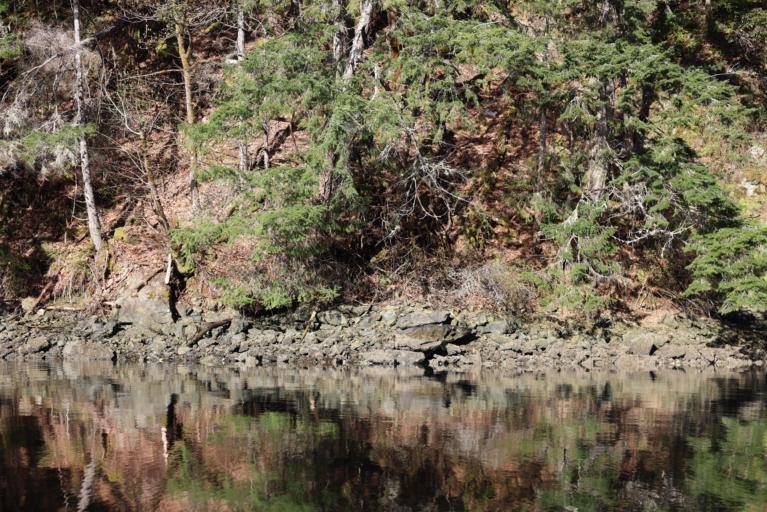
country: CA
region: British Columbia
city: North Saanich
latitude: 48.5640
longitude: -123.4761
